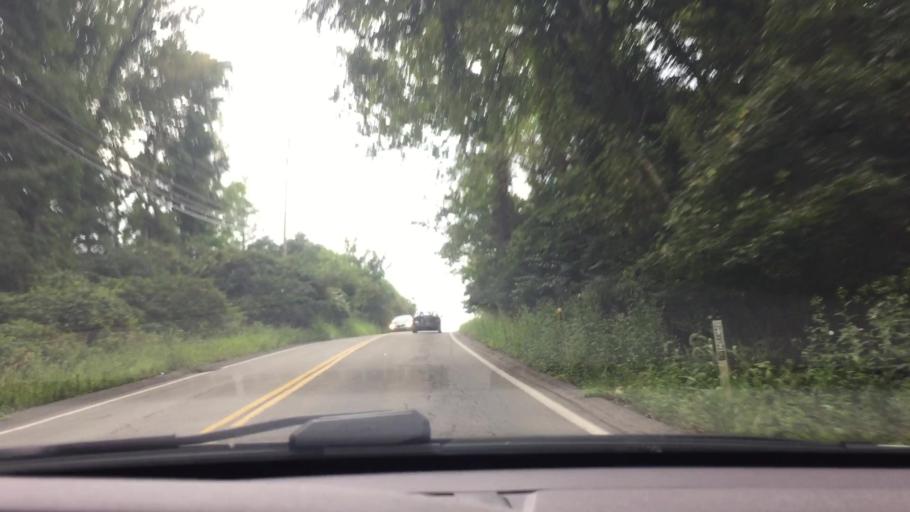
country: US
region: Pennsylvania
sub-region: Westmoreland County
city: Level Green
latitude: 40.4126
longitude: -79.7360
